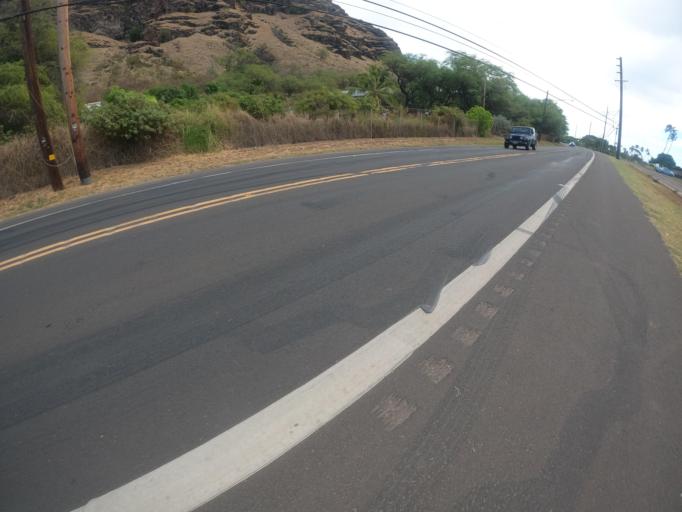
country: US
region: Hawaii
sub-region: Honolulu County
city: Makaha
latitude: 21.4881
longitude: -158.2294
